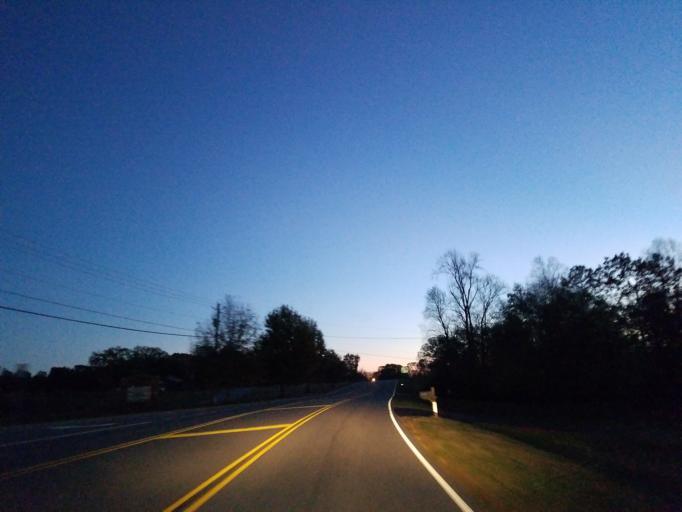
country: US
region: Georgia
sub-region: Dawson County
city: Dawsonville
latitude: 34.3283
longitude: -84.1043
